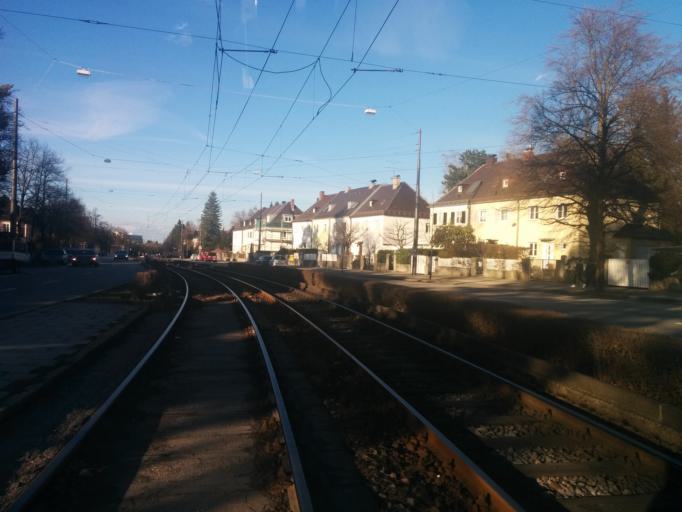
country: DE
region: Bavaria
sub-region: Upper Bavaria
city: Munich
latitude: 48.0924
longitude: 11.5629
